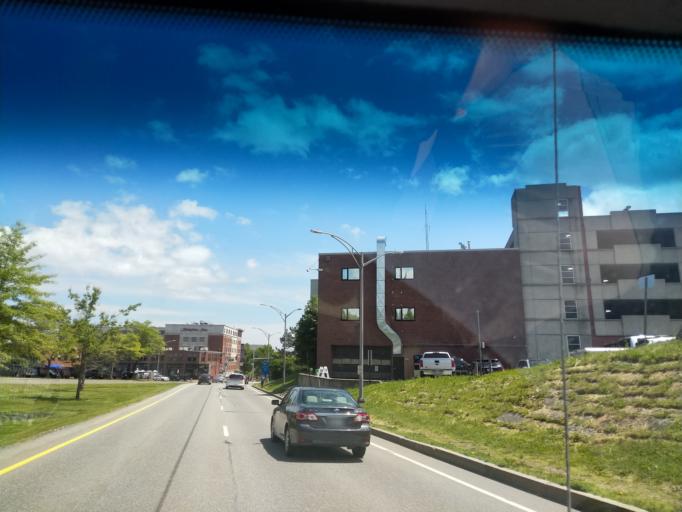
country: US
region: Maine
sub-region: Cumberland County
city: Portland
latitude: 43.6599
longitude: -70.2532
